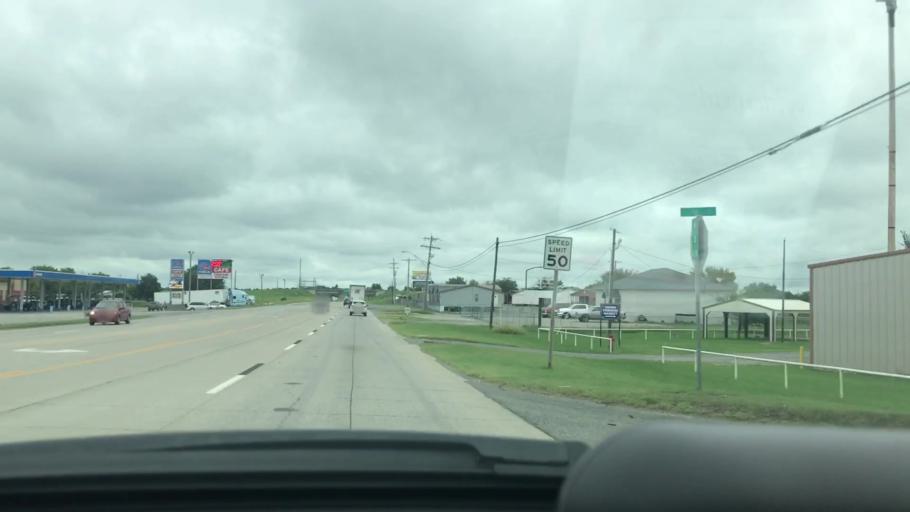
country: US
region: Oklahoma
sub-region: Pittsburg County
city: McAlester
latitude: 34.8321
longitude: -95.8400
